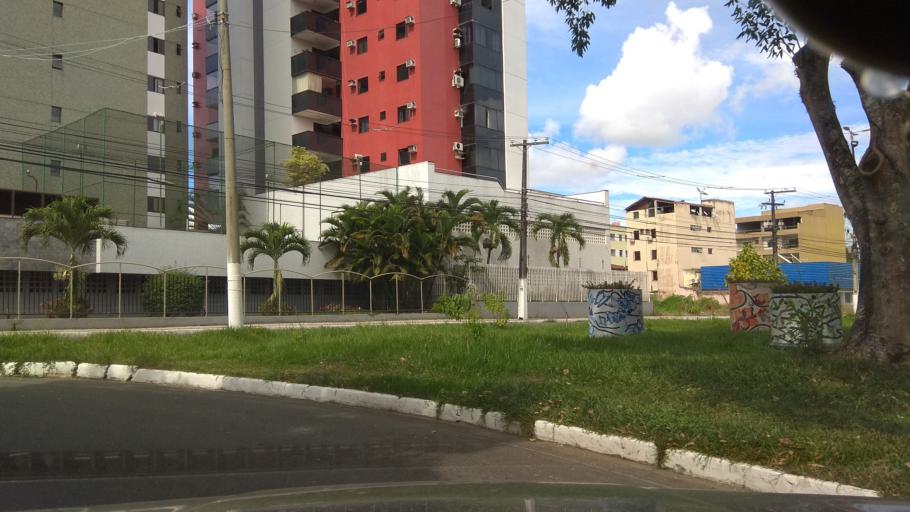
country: BR
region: Bahia
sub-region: Itabuna
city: Itabuna
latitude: -14.7990
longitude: -39.2759
